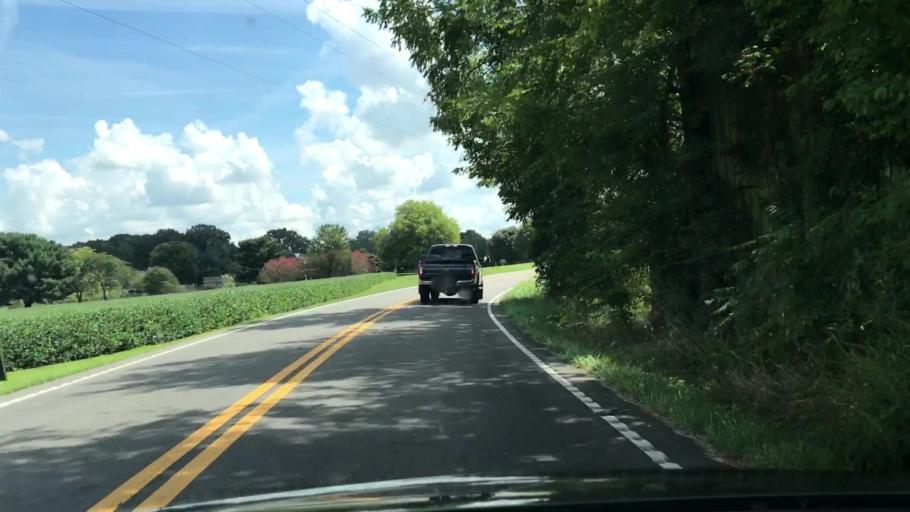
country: US
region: Tennessee
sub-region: Robertson County
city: Springfield
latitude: 36.5562
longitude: -86.8272
